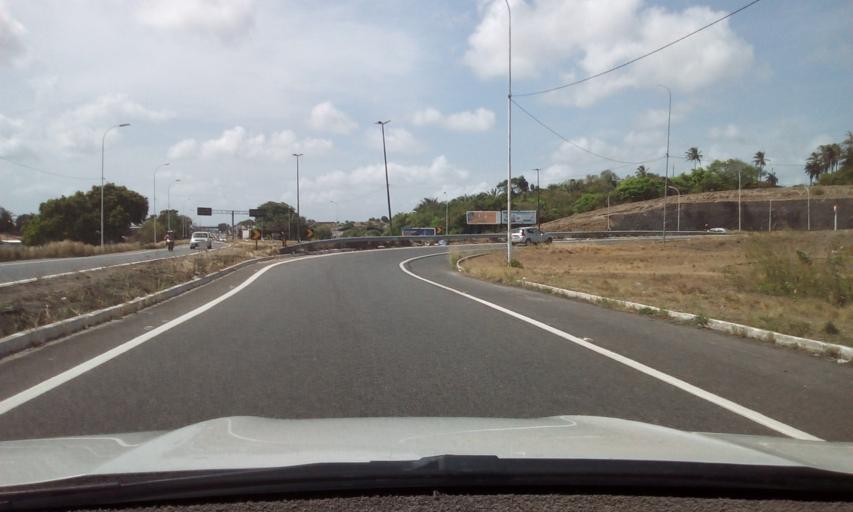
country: BR
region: Paraiba
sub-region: Bayeux
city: Bayeux
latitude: -7.1663
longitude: -34.8980
